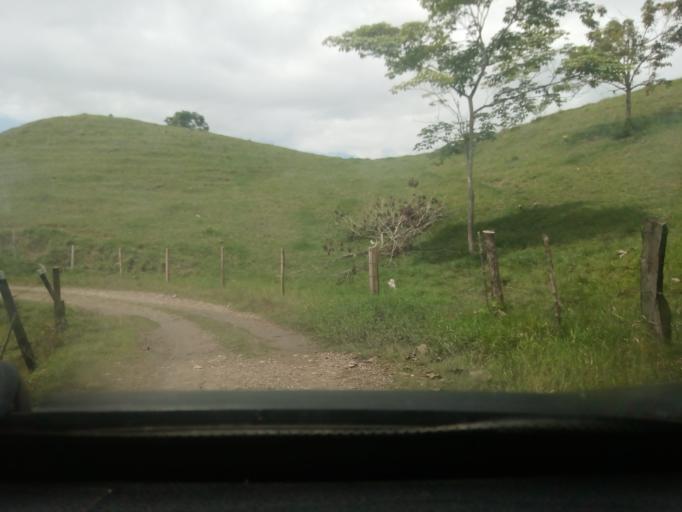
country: CO
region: Boyaca
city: Puerto Boyaca
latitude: 6.0106
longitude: -74.3880
